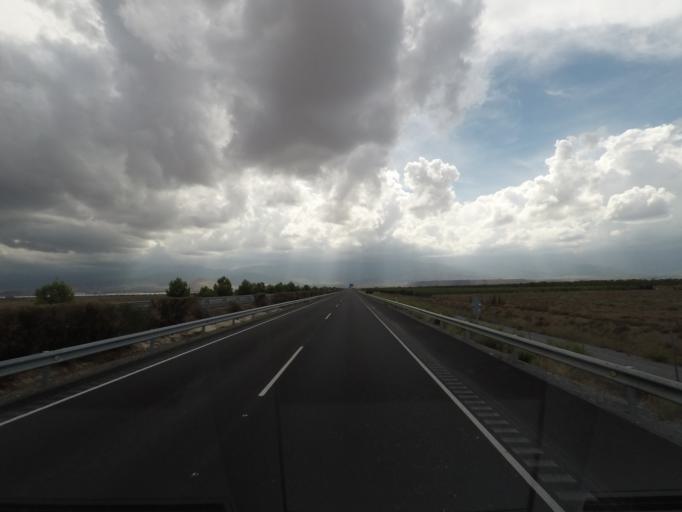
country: ES
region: Andalusia
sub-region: Provincia de Granada
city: Albunan
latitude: 37.2438
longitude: -3.0819
